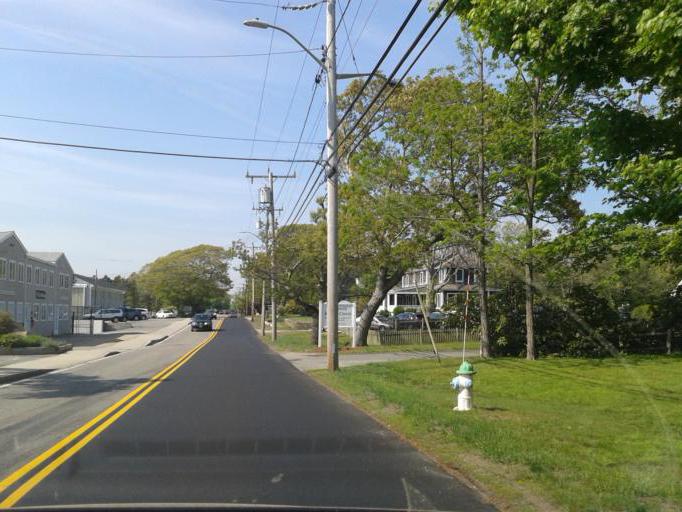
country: US
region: Massachusetts
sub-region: Barnstable County
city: Falmouth
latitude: 41.5495
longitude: -70.6000
